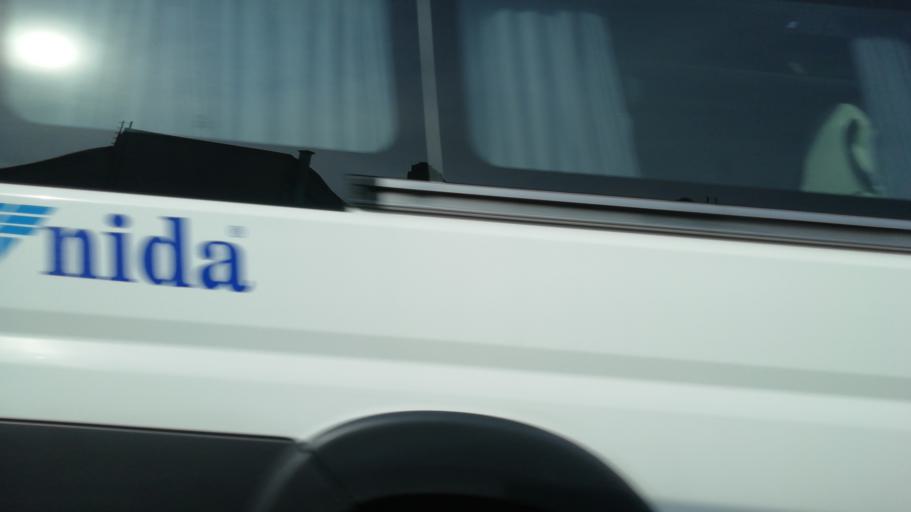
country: TR
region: Istanbul
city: Basaksehir
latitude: 41.0962
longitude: 28.7934
